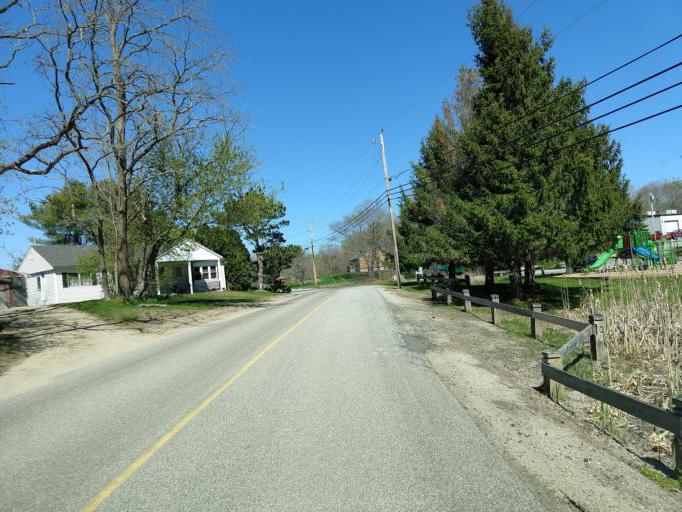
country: US
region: Maine
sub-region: York County
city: Arundel
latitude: 43.3860
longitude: -70.4630
